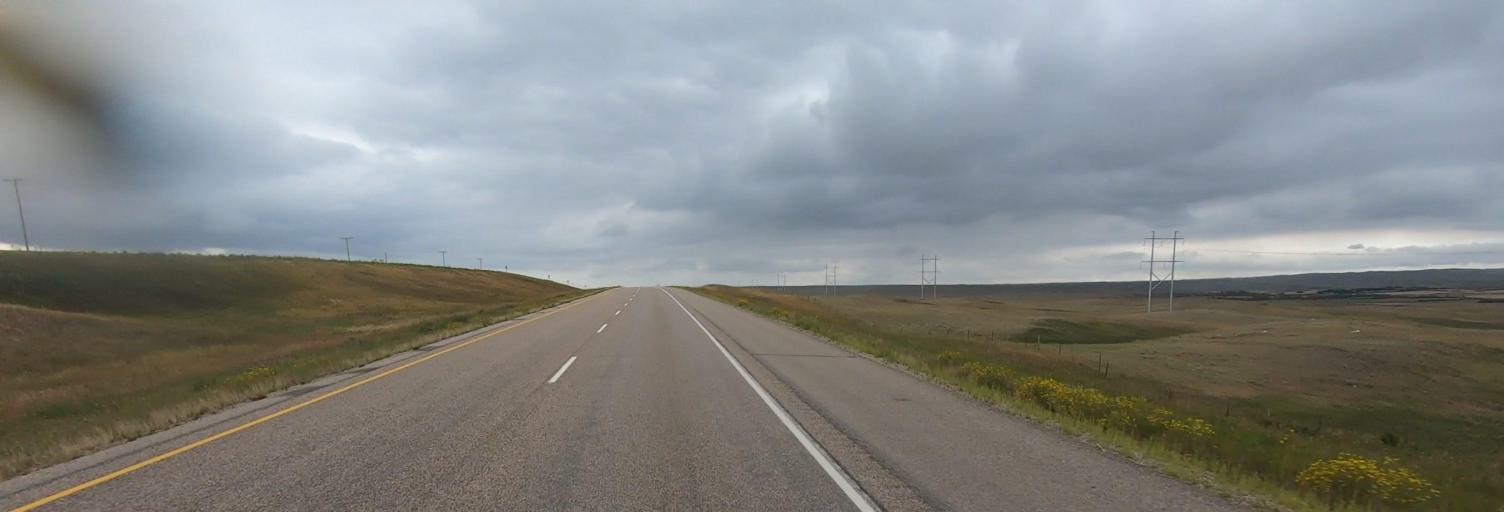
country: CA
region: Saskatchewan
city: Gravelbourg
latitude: 50.4644
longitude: -106.3287
